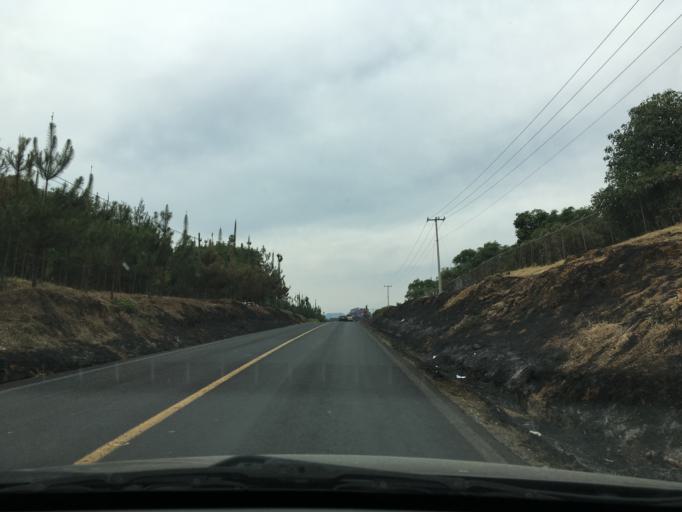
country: MX
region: Michoacan
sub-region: Uruapan
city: Uruapan
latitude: 19.3835
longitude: -102.0922
